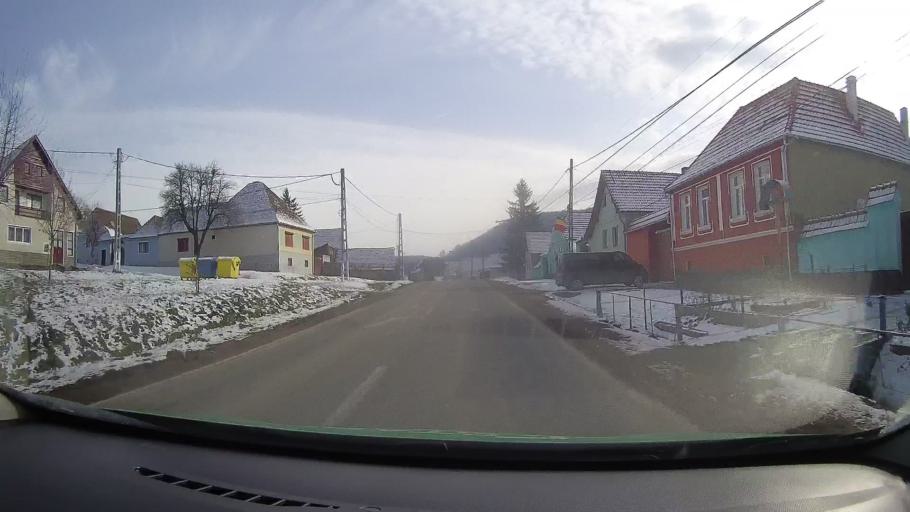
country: RO
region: Mures
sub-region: Comuna Apold
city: Saes
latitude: 46.1511
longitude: 24.7710
